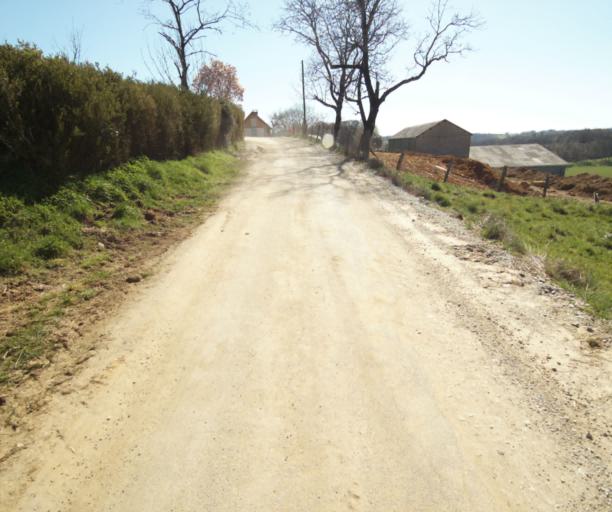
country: FR
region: Limousin
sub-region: Departement de la Correze
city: Seilhac
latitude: 45.3481
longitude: 1.7269
